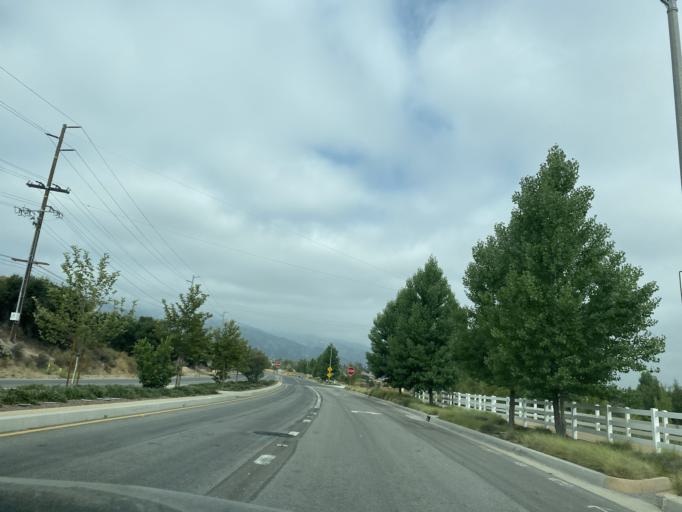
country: US
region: California
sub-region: Riverside County
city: El Cerrito
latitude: 33.7626
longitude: -117.4650
